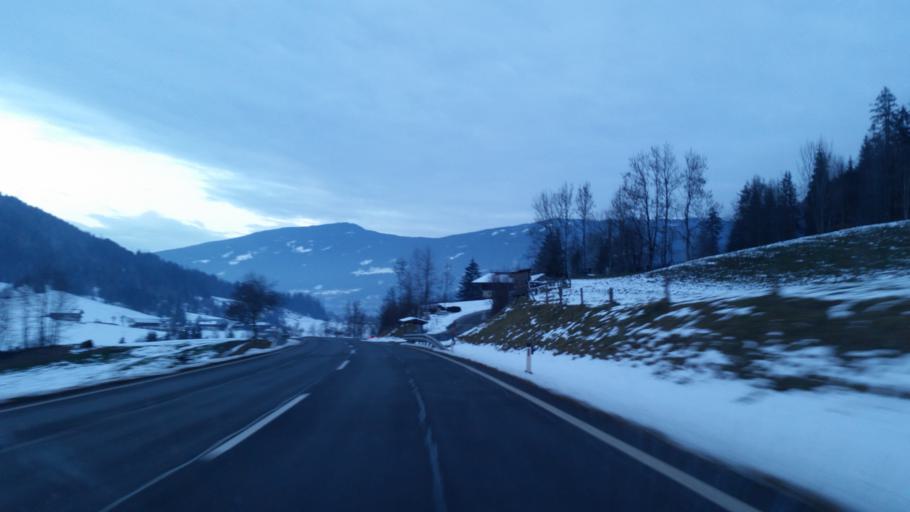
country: AT
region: Salzburg
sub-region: Politischer Bezirk Sankt Johann im Pongau
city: Forstau
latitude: 47.3531
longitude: 13.4993
